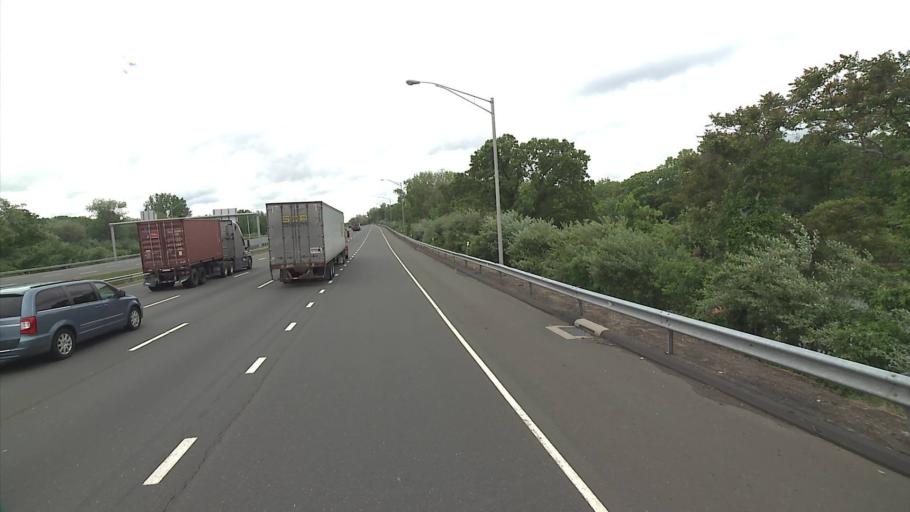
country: US
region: Connecticut
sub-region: New Haven County
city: North Haven
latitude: 41.3721
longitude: -72.8698
